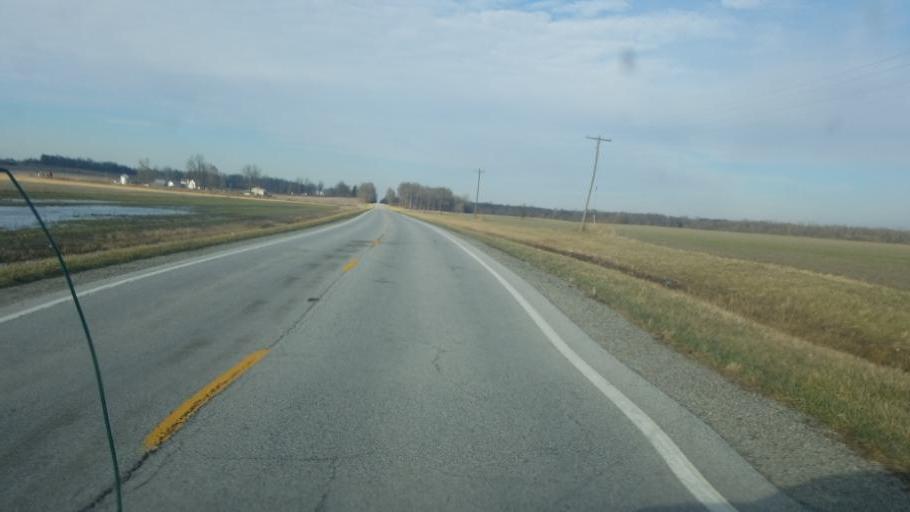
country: US
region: Illinois
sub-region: Wabash County
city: Mount Carmel
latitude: 38.5508
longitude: -87.6949
